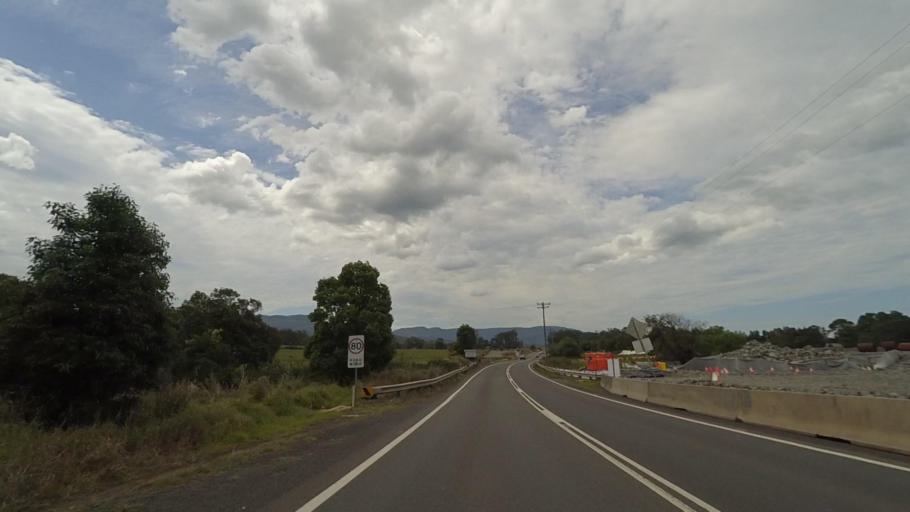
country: AU
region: New South Wales
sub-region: Shoalhaven Shire
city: Berry
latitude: -34.7895
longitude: 150.6730
